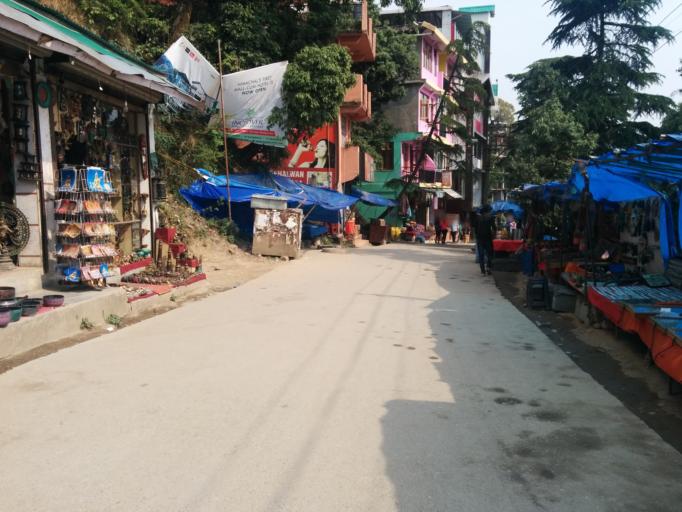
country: IN
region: Himachal Pradesh
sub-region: Kangra
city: Dharmsala
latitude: 32.2351
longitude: 76.3242
